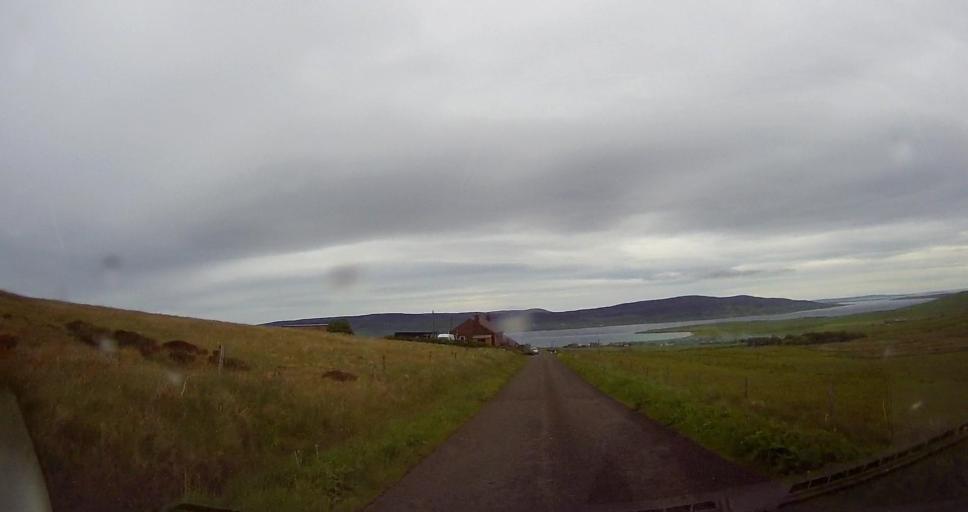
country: GB
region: Scotland
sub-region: Orkney Islands
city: Orkney
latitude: 59.1065
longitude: -3.1262
